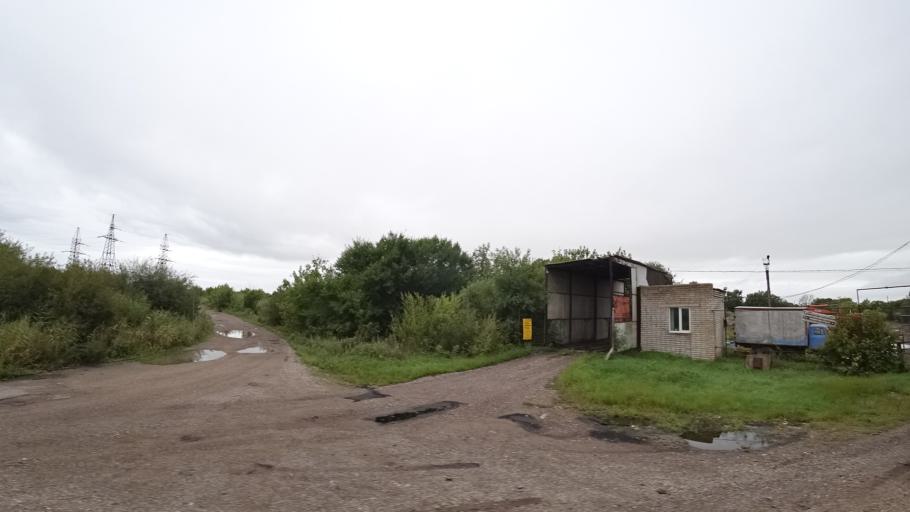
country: RU
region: Primorskiy
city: Chernigovka
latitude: 44.3339
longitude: 132.5227
